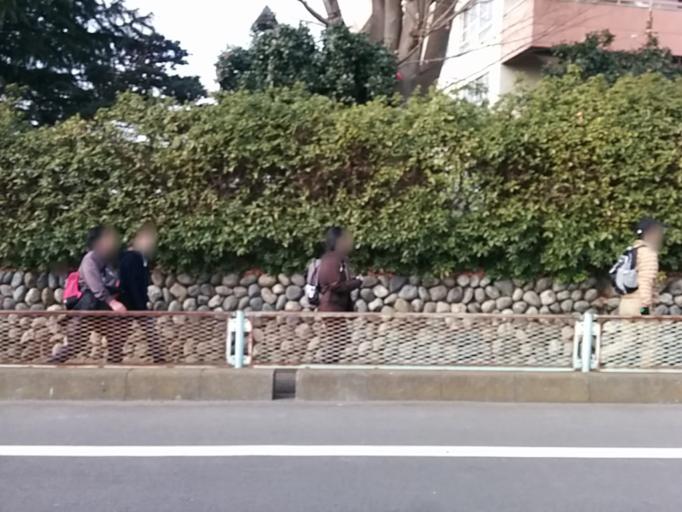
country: JP
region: Saitama
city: Kawagoe
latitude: 35.9135
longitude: 139.4913
